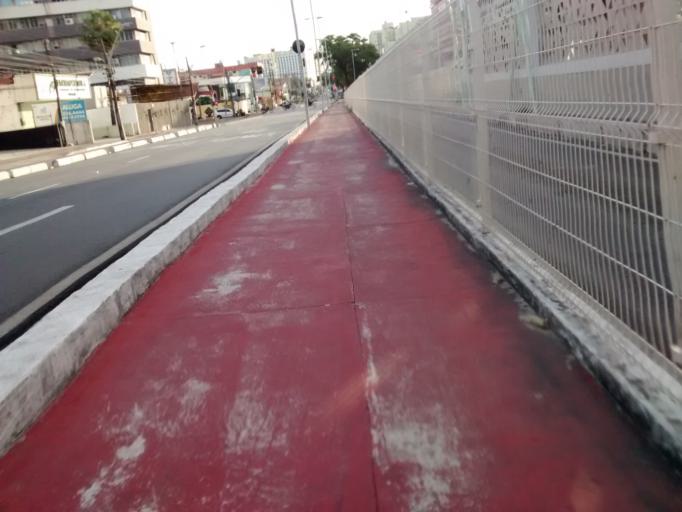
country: BR
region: Ceara
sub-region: Fortaleza
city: Fortaleza
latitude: -3.7352
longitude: -38.5621
